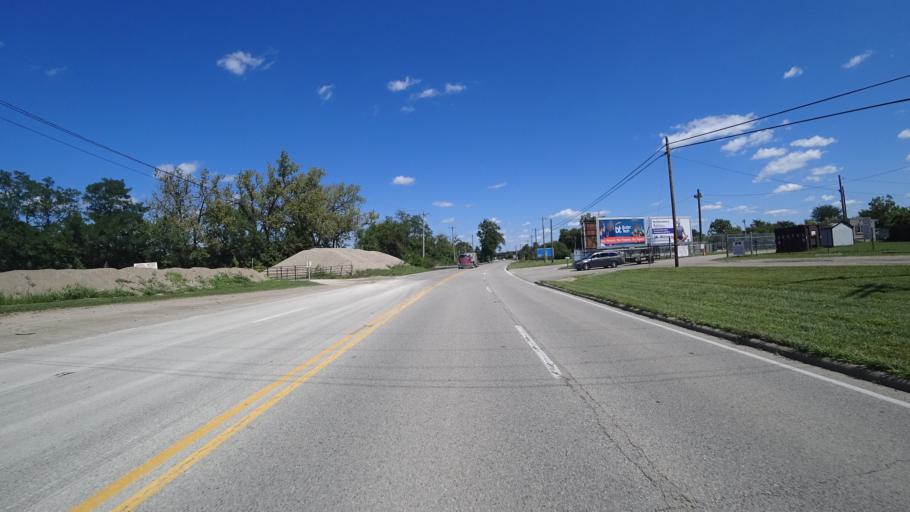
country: US
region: Ohio
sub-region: Butler County
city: Hamilton
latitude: 39.4132
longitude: -84.5532
